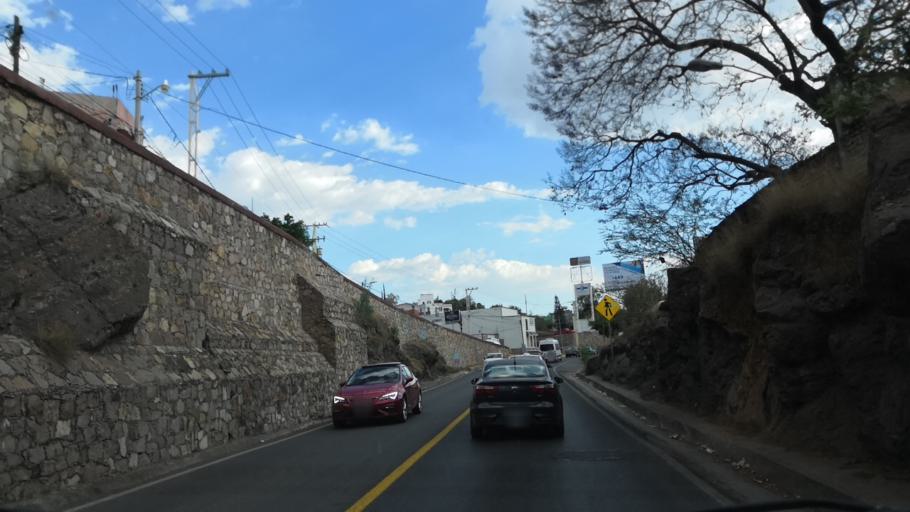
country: MX
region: Guanajuato
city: Marfil
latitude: 20.9968
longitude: -101.2852
